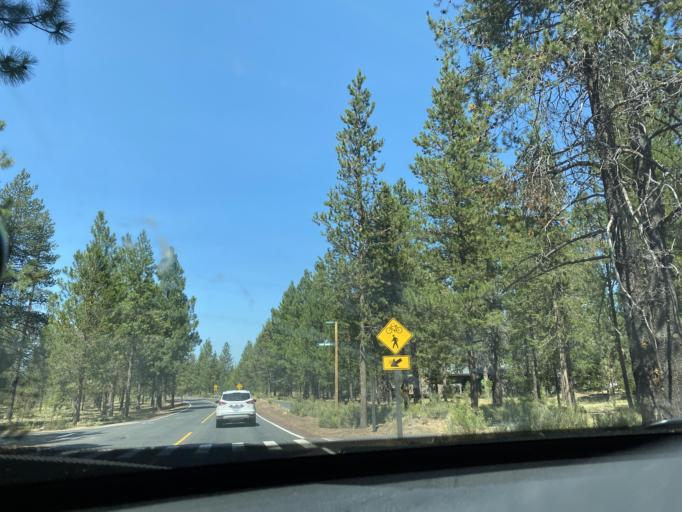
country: US
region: Oregon
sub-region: Deschutes County
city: Sunriver
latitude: 43.8894
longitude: -121.4359
